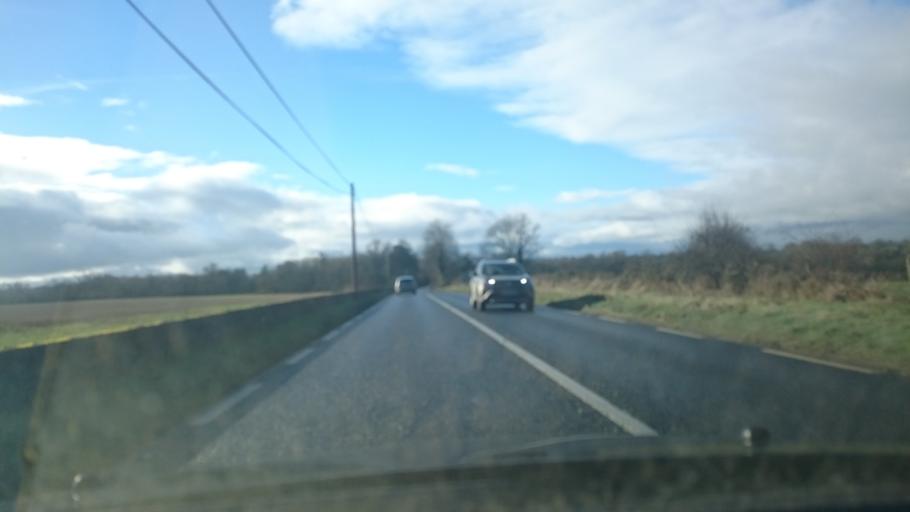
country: IE
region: Leinster
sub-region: Kilkenny
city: Callan
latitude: 52.5820
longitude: -7.3159
